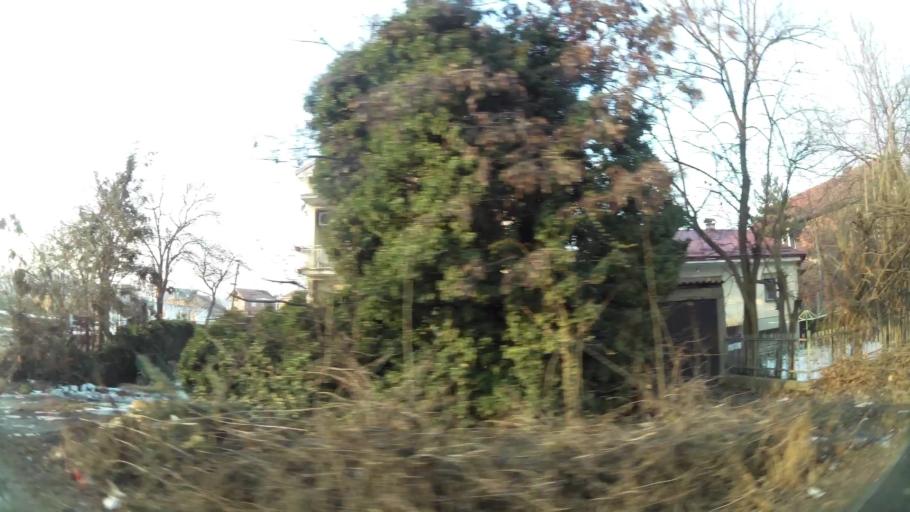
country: MK
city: Creshevo
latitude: 42.0122
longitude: 21.5128
